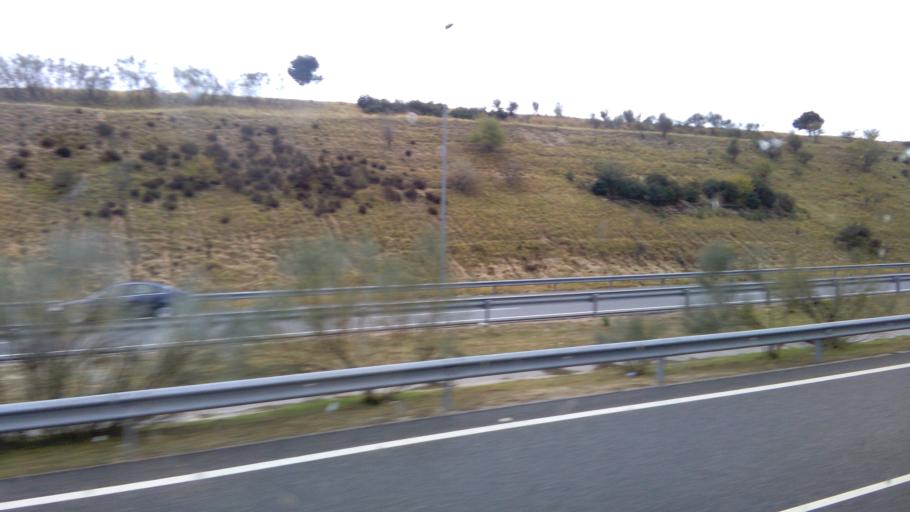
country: ES
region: Madrid
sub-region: Provincia de Madrid
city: Alcorcon
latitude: 40.3421
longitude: -3.7937
